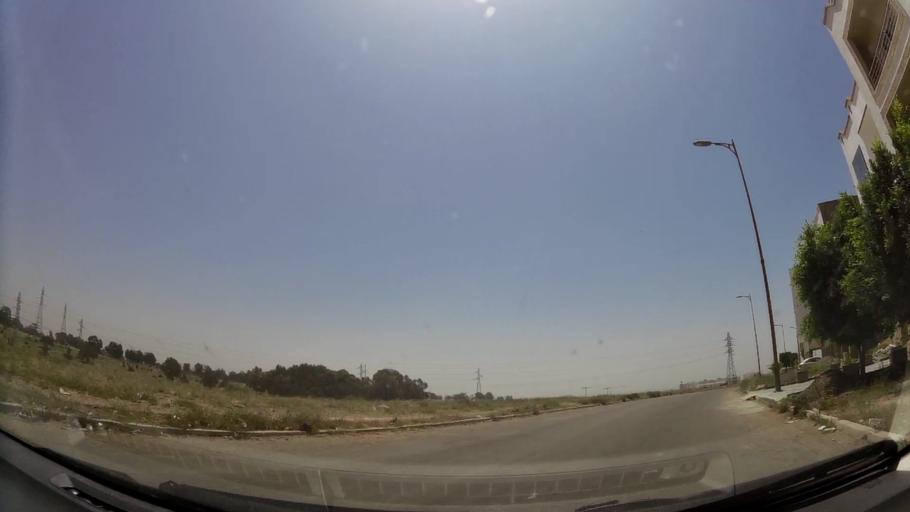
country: MA
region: Oued ed Dahab-Lagouira
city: Dakhla
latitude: 30.4263
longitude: -9.5524
